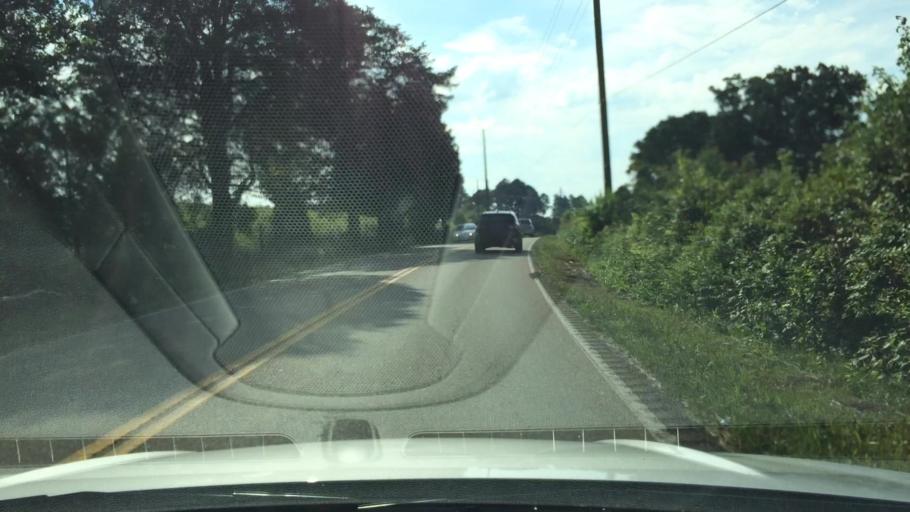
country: US
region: Tennessee
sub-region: Sevier County
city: Sevierville
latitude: 35.9236
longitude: -83.5979
